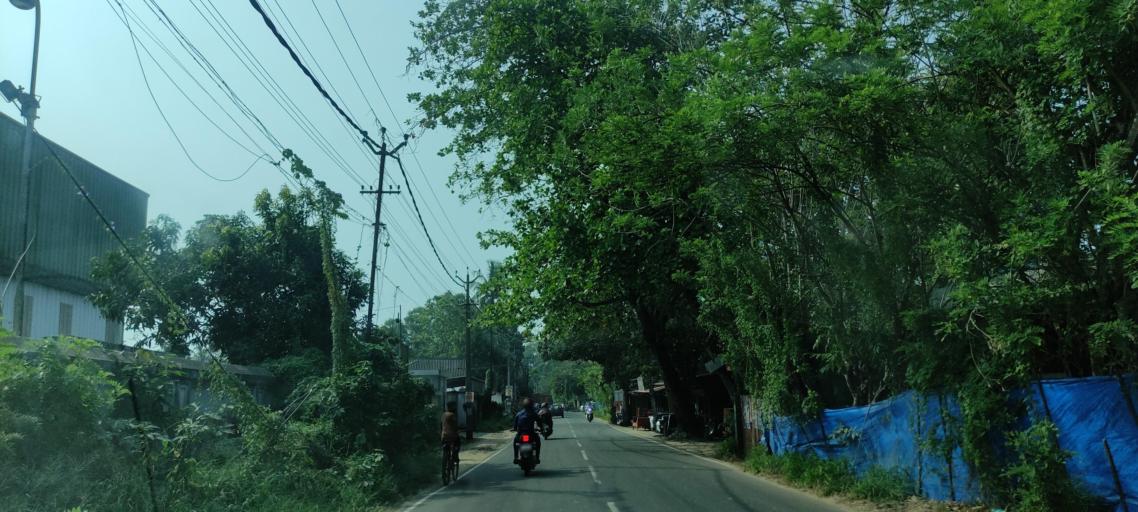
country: IN
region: Kerala
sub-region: Alappuzha
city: Vayalar
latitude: 9.6958
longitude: 76.3245
